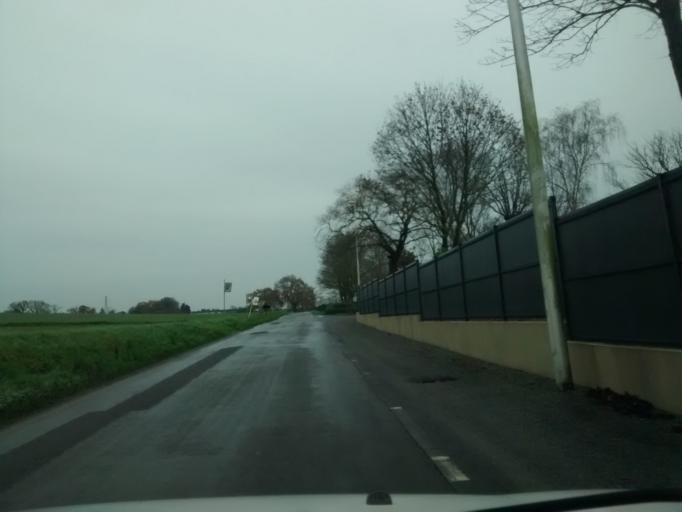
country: FR
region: Brittany
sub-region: Departement d'Ille-et-Vilaine
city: Acigne
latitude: 48.1376
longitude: -1.5477
